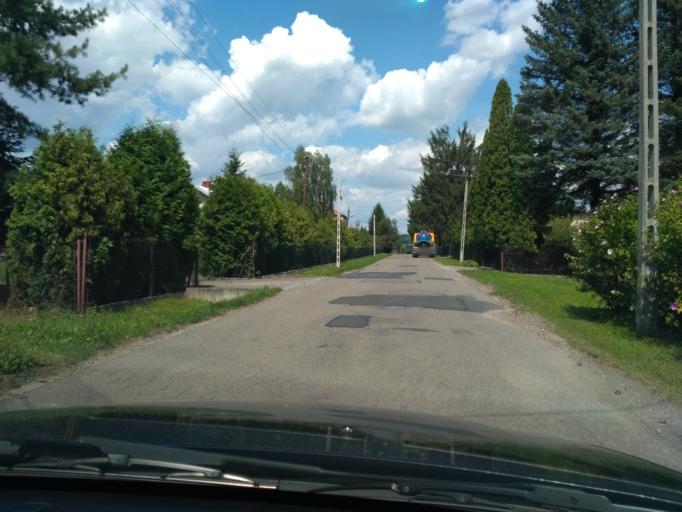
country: PL
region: Subcarpathian Voivodeship
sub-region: Powiat strzyzowski
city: Strzyzow
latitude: 49.8795
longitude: 21.7557
